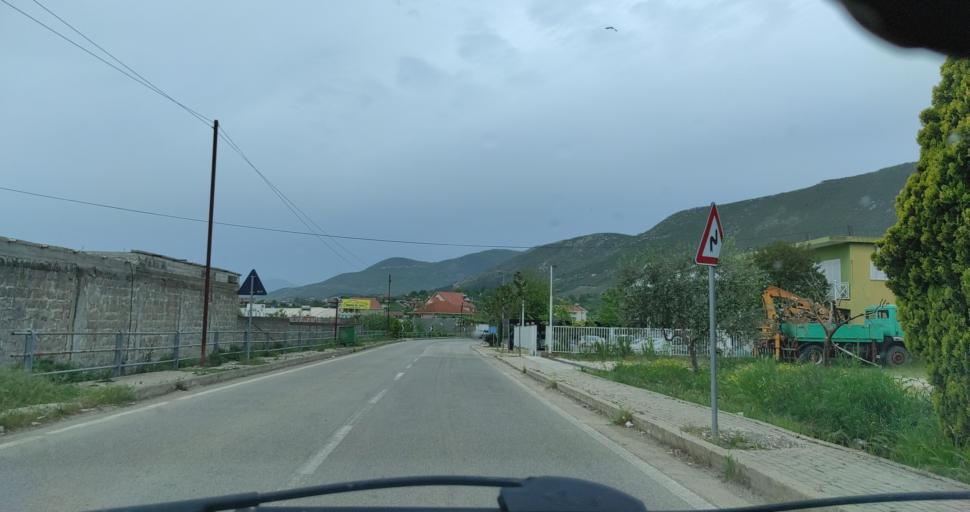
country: AL
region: Lezhe
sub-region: Rrethi i Kurbinit
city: Lac
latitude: 41.6074
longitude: 19.7124
